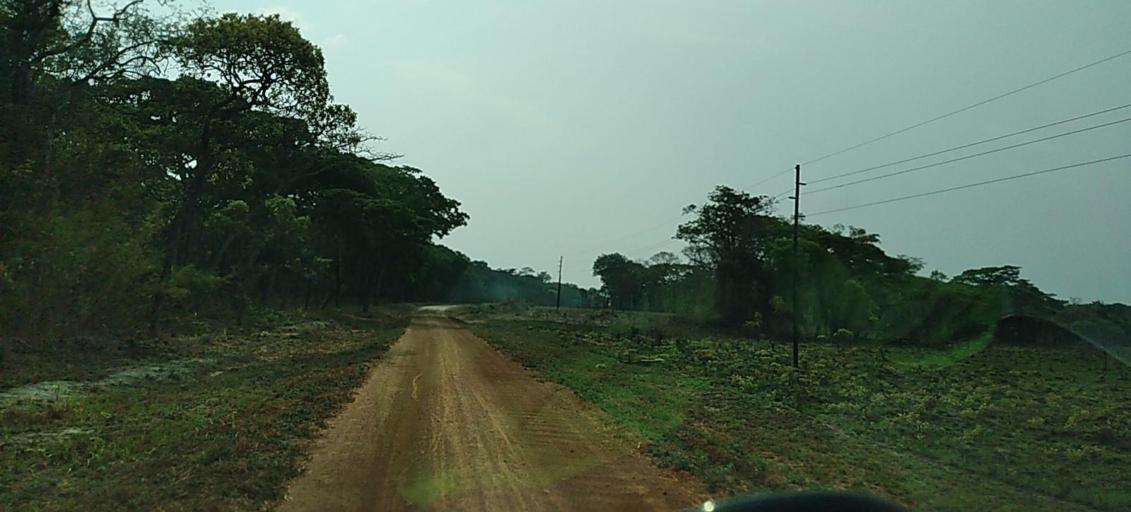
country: ZM
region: North-Western
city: Solwezi
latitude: -12.6948
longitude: 26.4052
